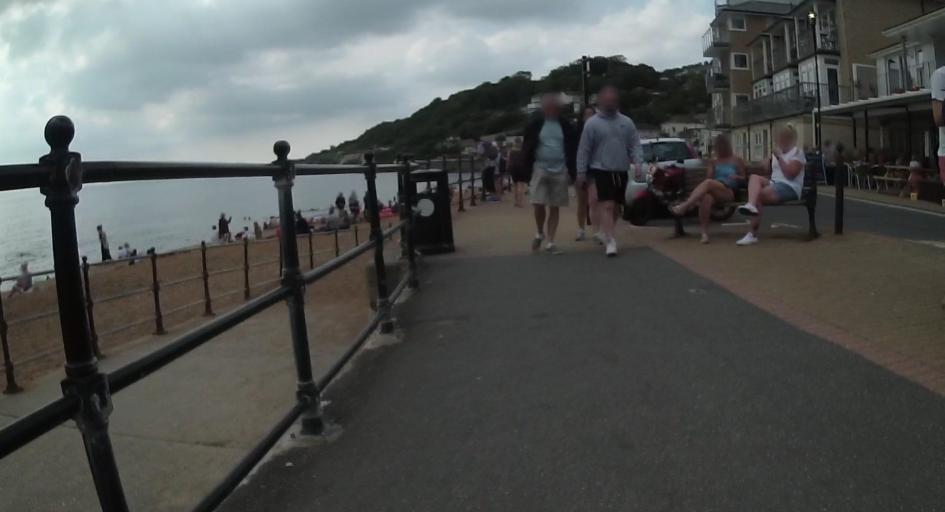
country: GB
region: England
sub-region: Isle of Wight
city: Ventnor
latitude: 50.5925
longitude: -1.2071
